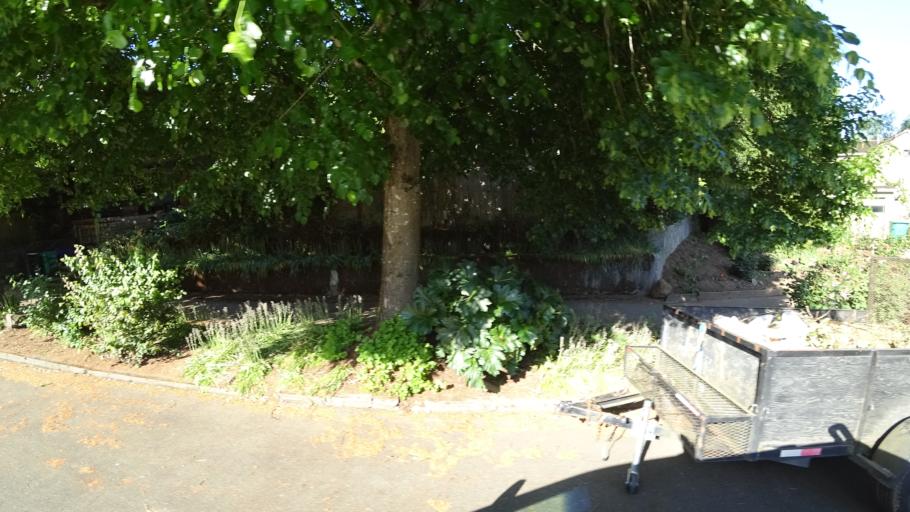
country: US
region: Oregon
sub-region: Multnomah County
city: Portland
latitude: 45.5513
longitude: -122.6858
